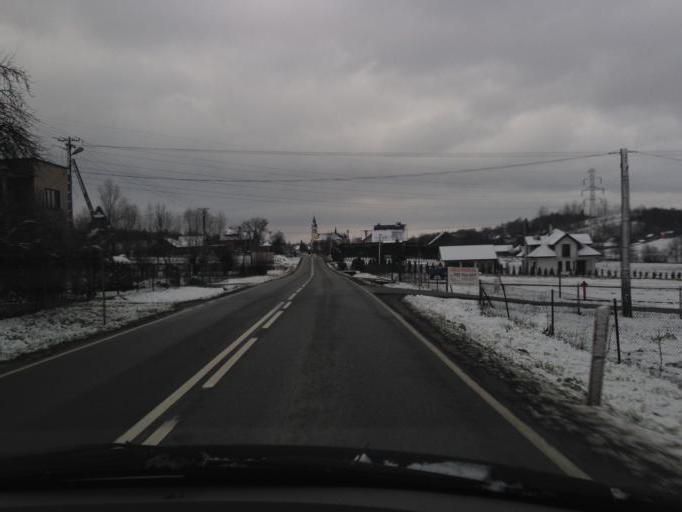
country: PL
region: Lesser Poland Voivodeship
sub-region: Powiat tarnowski
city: Siemiechow
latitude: 49.8541
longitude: 20.8914
